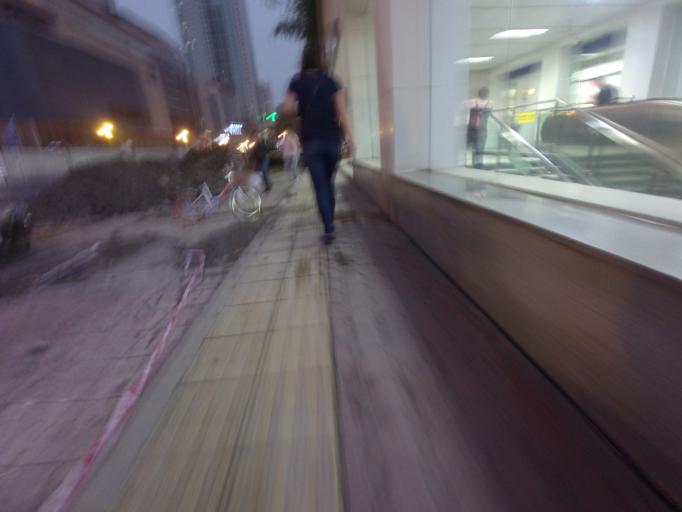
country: CN
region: Sichuan
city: Chengdu
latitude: 30.6695
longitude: 104.0648
